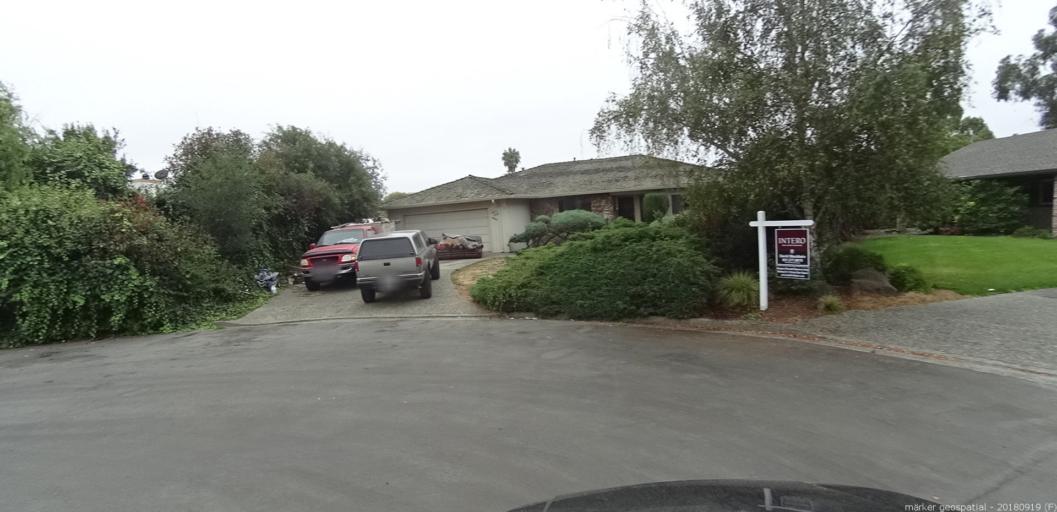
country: US
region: California
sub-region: Monterey County
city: Castroville
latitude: 36.7788
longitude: -121.7247
